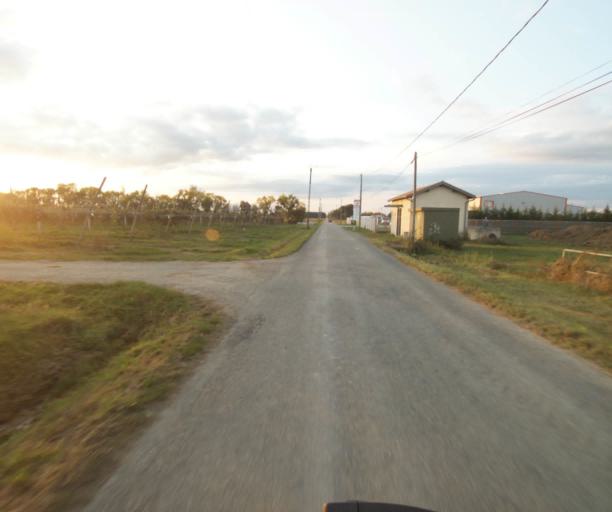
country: FR
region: Midi-Pyrenees
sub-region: Departement du Tarn-et-Garonne
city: Verdun-sur-Garonne
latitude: 43.8221
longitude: 1.2417
